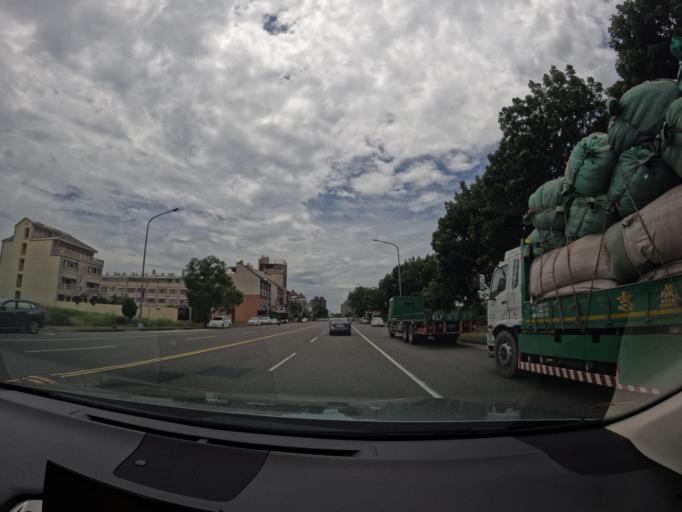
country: TW
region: Kaohsiung
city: Kaohsiung
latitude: 22.7270
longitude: 120.2932
